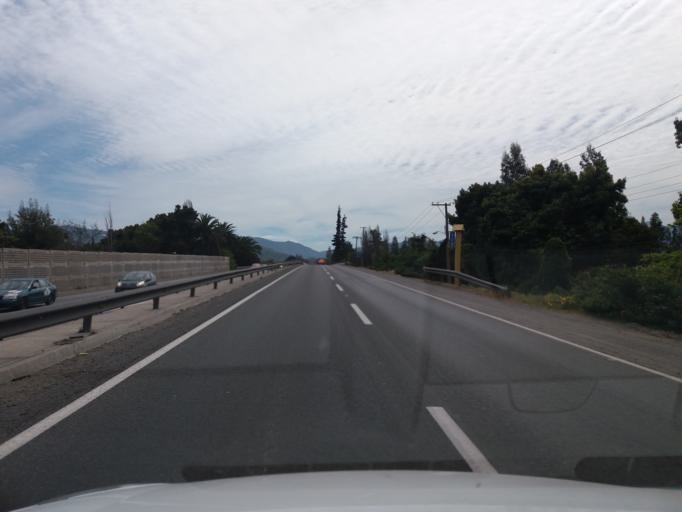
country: CL
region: Valparaiso
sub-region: Provincia de Quillota
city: Hacienda La Calera
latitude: -32.7348
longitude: -71.1999
